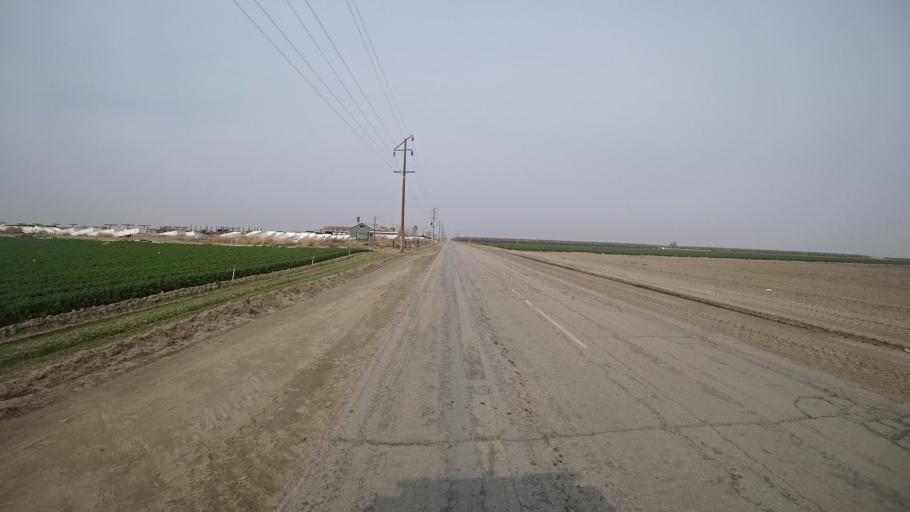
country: US
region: California
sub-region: Kern County
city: Arvin
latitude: 35.1611
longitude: -118.8781
